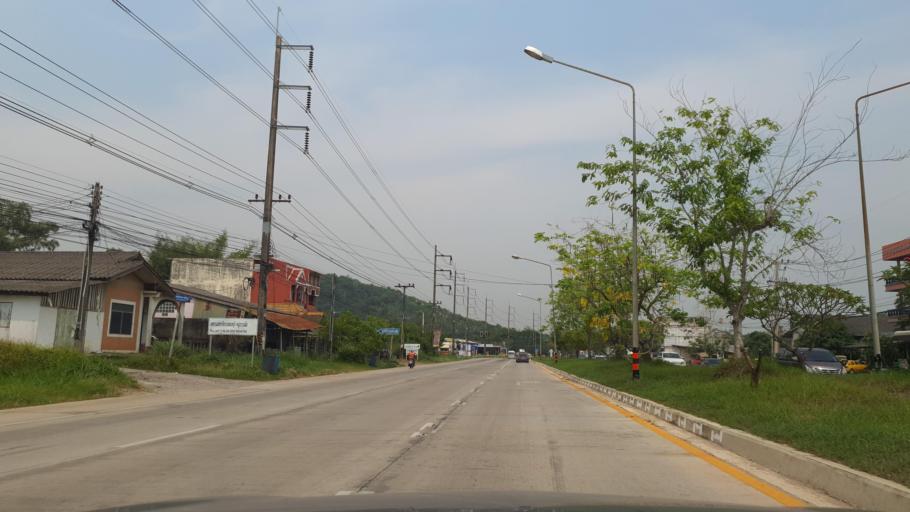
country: TH
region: Rayong
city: Rayong
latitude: 12.6422
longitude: 101.4205
